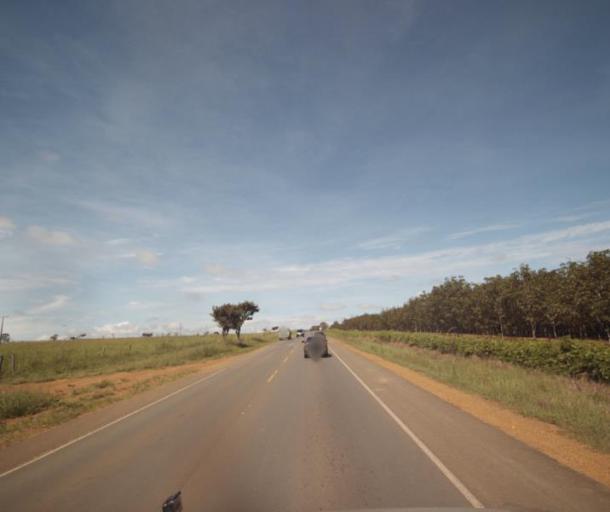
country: BR
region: Goias
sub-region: Anapolis
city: Anapolis
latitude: -16.1940
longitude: -48.9073
